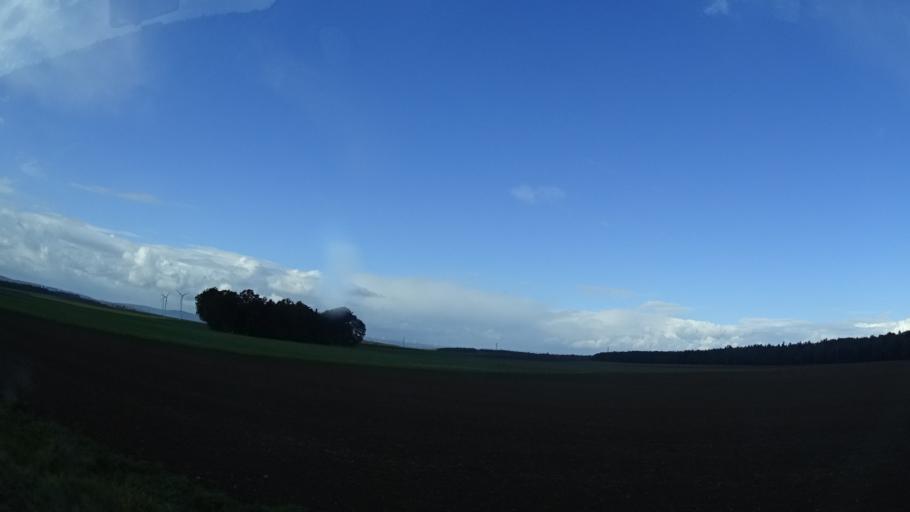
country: DE
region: Baden-Wuerttemberg
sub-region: Karlsruhe Region
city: Hopfingen
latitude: 49.6298
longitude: 9.4176
